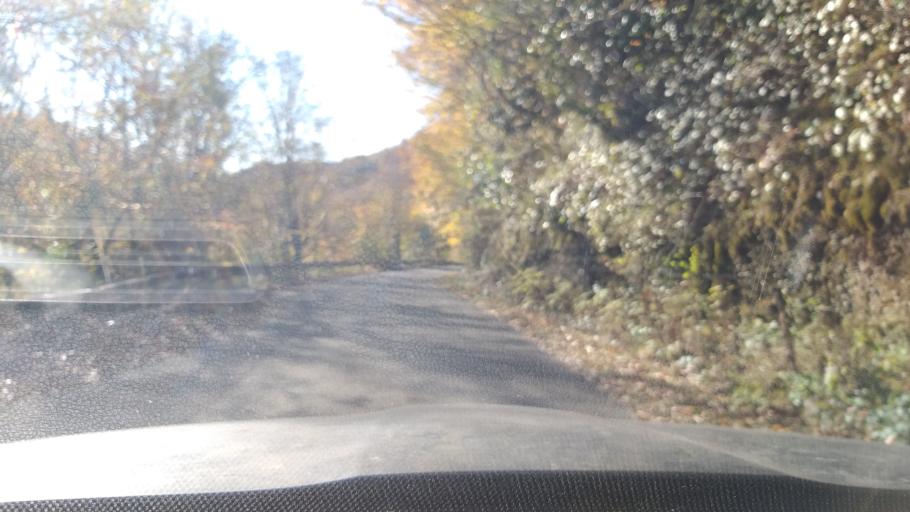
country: GE
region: Abkhazia
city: Bich'vinta
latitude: 43.1921
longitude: 40.4555
